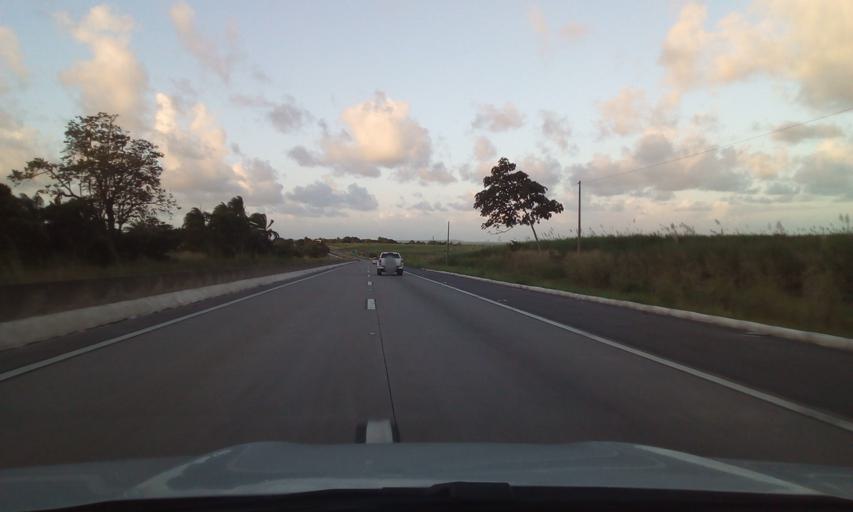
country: BR
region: Pernambuco
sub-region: Itapissuma
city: Itapissuma
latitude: -7.7113
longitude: -34.9313
